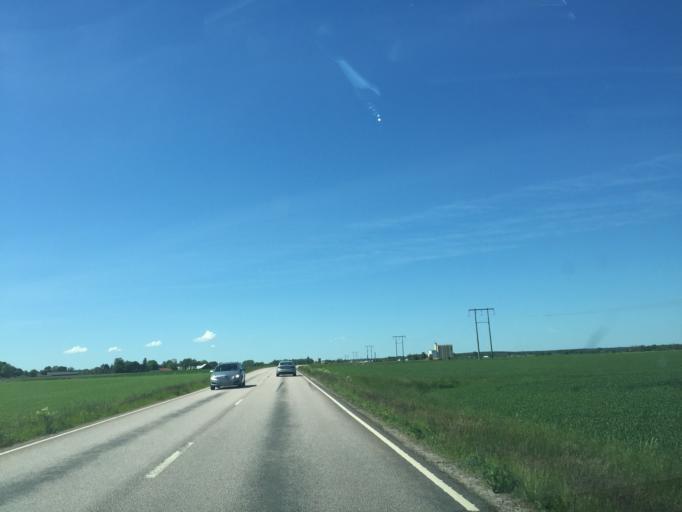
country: SE
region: OEstergoetland
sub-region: Mjolby Kommun
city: Mjolby
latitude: 58.3876
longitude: 15.1303
